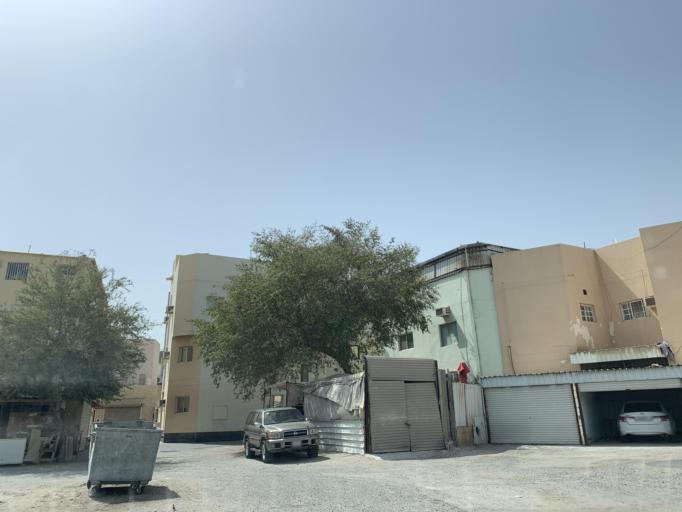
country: BH
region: Manama
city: Manama
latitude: 26.2100
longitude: 50.5855
